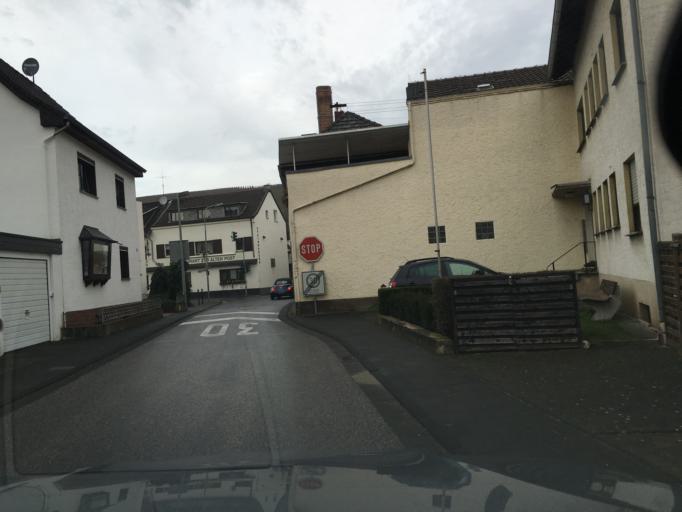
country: DE
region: Rheinland-Pfalz
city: Schalkenbach
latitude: 50.5505
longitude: 7.1646
